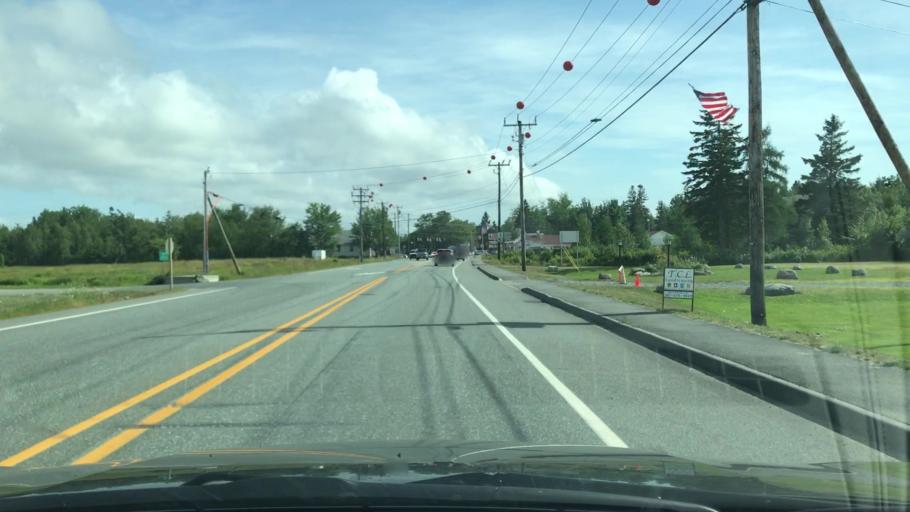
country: US
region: Maine
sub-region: Hancock County
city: Trenton
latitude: 44.4419
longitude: -68.3700
